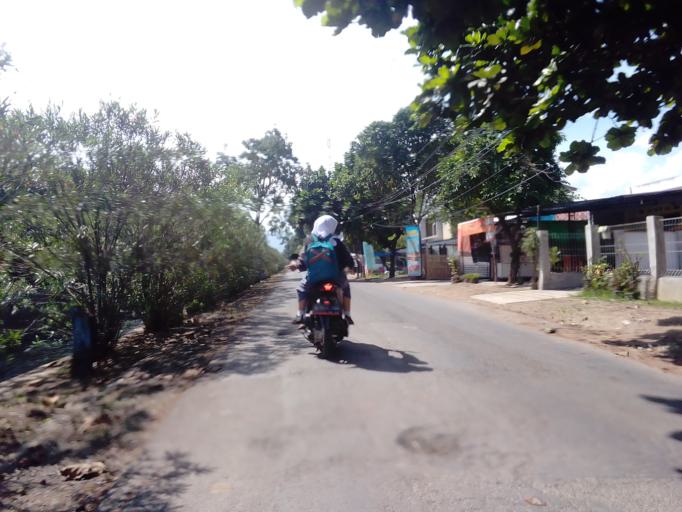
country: ID
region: West Java
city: Bandung
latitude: -6.9421
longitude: 107.6697
